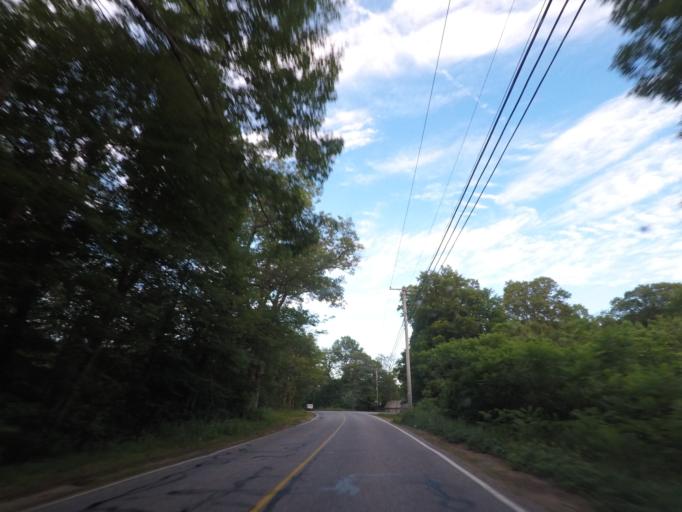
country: US
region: Massachusetts
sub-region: Worcester County
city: Warren
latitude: 42.1915
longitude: -72.1796
